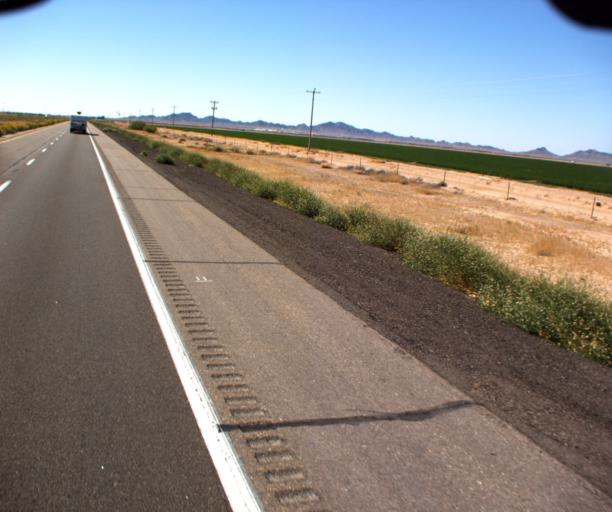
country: US
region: Arizona
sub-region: Maricopa County
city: Gila Bend
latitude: 32.9153
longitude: -112.9319
